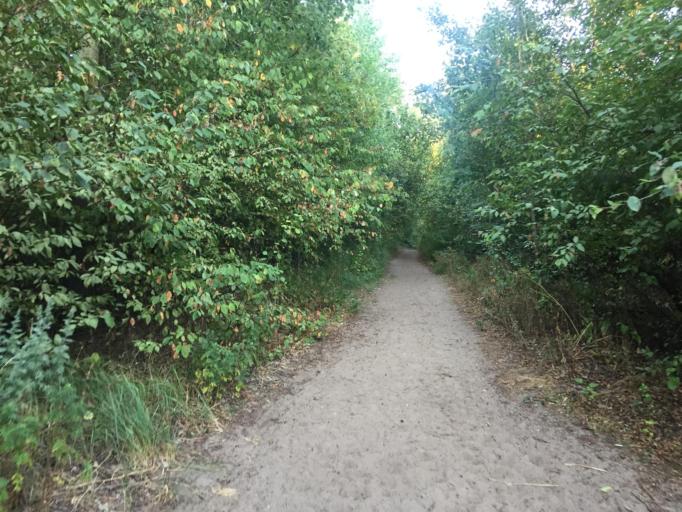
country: RU
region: St.-Petersburg
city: Kronshtadt
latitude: 60.0264
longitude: 29.6703
